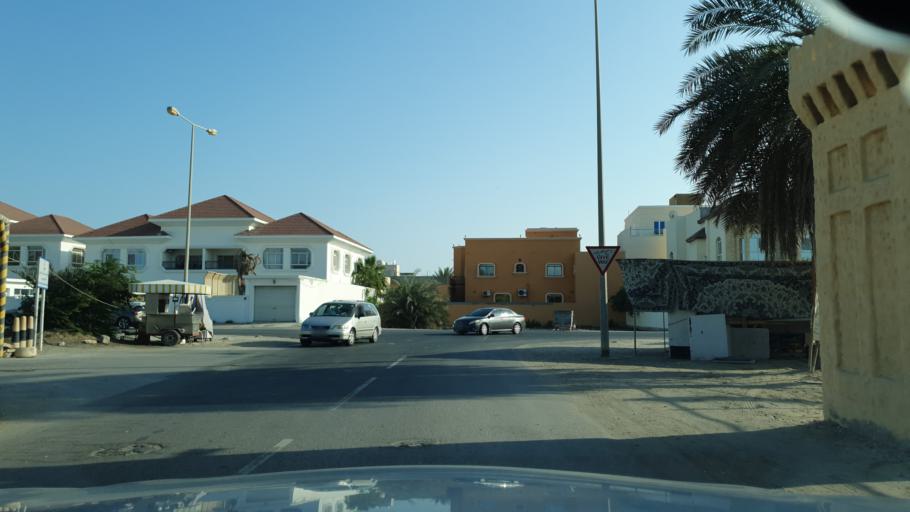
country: BH
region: Manama
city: Jidd Hafs
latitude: 26.2235
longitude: 50.4601
